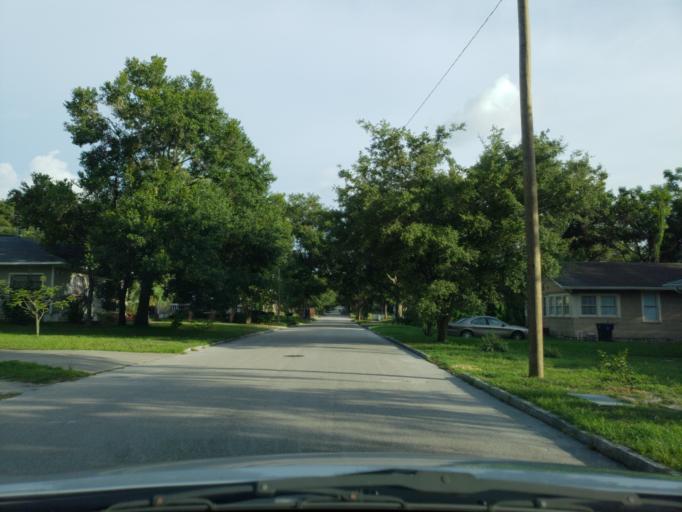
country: US
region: Florida
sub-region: Hillsborough County
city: Tampa
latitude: 27.9934
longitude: -82.4584
